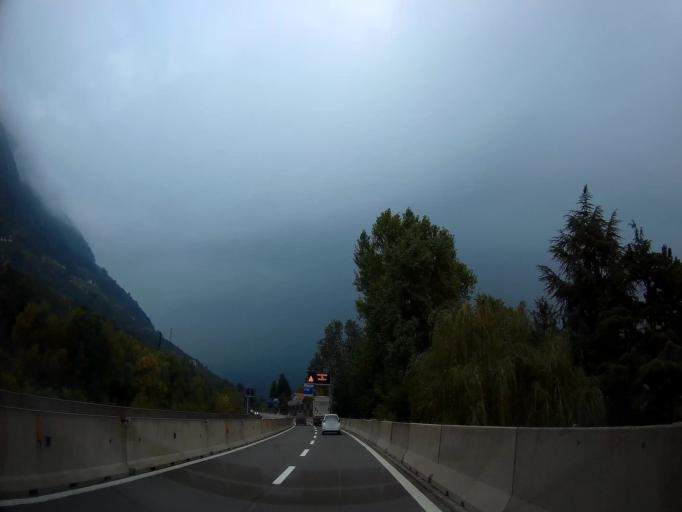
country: IT
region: Trentino-Alto Adige
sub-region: Bolzano
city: Marlengo
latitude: 46.6646
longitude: 11.1437
